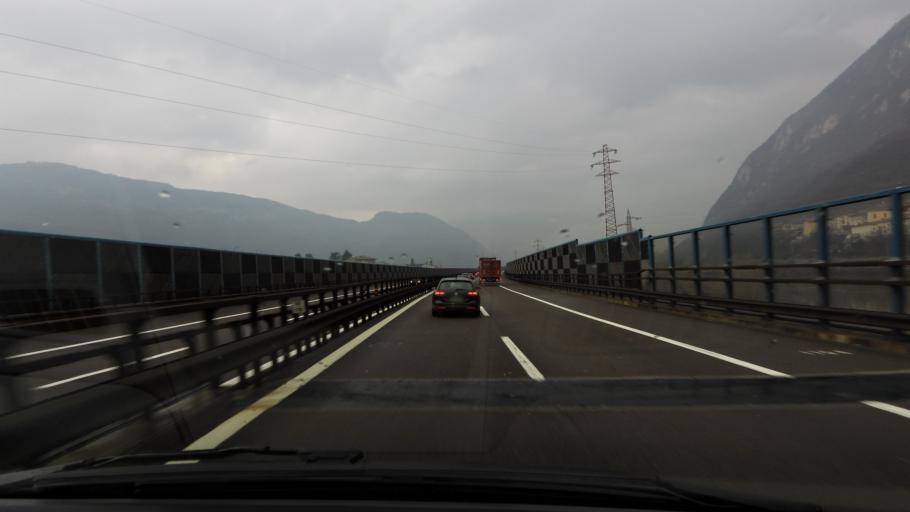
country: IT
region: Trentino-Alto Adige
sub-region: Provincia di Trento
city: Marco
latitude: 45.8109
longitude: 11.0112
